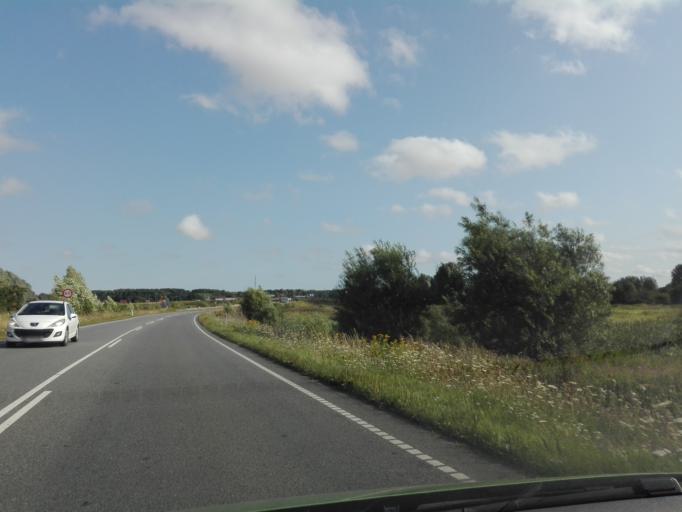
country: DK
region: Central Jutland
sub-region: Arhus Kommune
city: Lystrup
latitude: 56.2180
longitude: 10.2337
